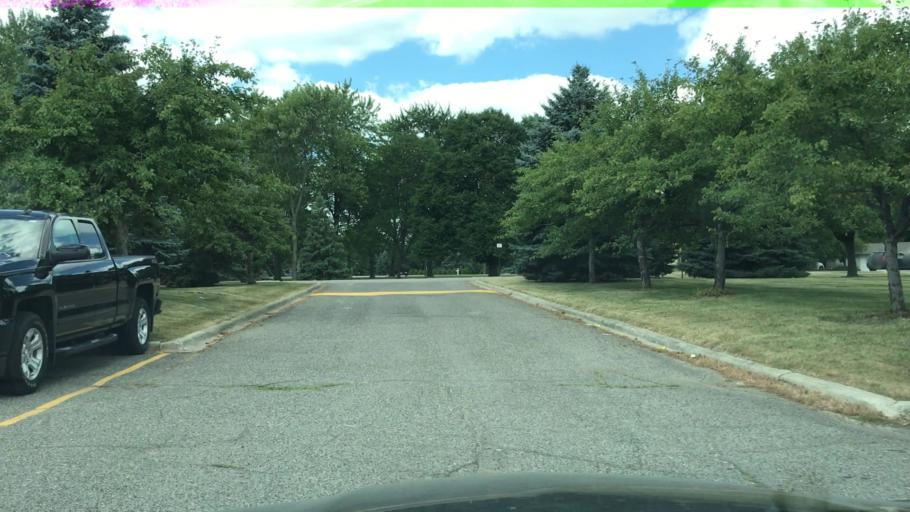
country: US
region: Michigan
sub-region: Oakland County
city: Madison Heights
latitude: 42.5262
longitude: -83.0757
